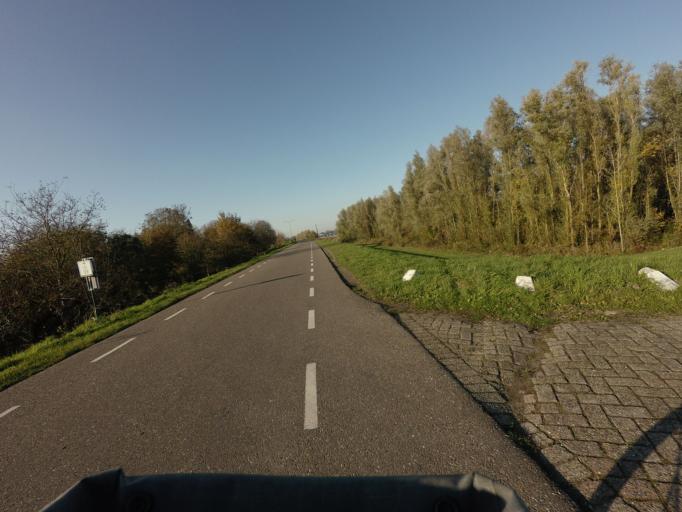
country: NL
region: North Brabant
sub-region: Gemeente Woudrichem
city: Woudrichem
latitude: 51.8031
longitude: 5.0199
